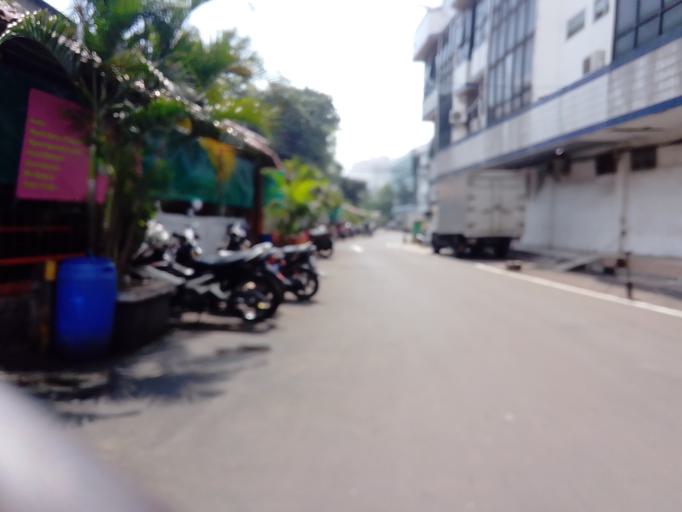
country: ID
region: Jakarta Raya
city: Jakarta
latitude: -6.1373
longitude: 106.8280
